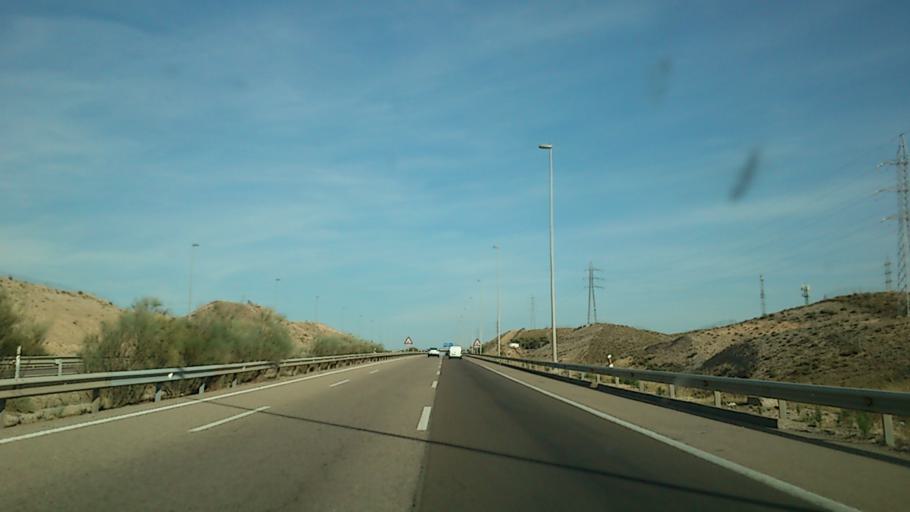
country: ES
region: Aragon
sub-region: Provincia de Zaragoza
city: Cuarte de Huerva
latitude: 41.6078
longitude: -0.9123
